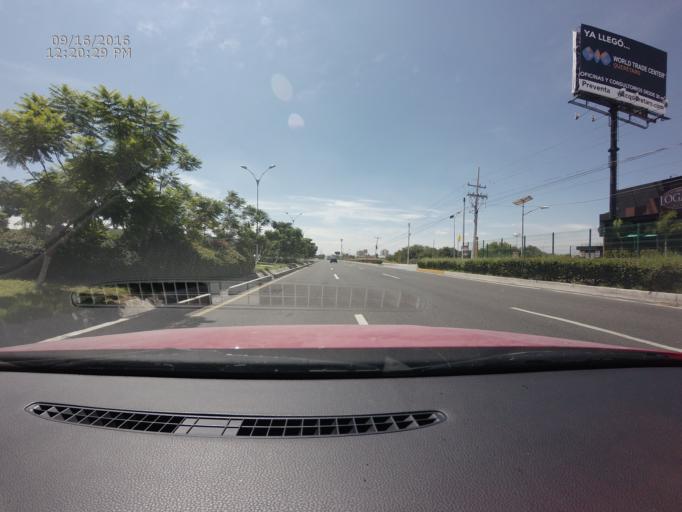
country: MX
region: Queretaro
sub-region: Queretaro
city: El Salitre
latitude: 20.6627
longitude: -100.4331
